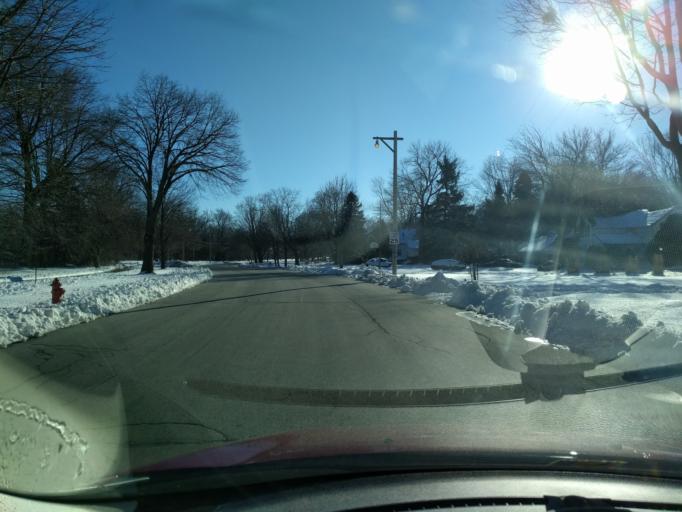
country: US
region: Wisconsin
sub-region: Milwaukee County
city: Glendale
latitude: 43.1140
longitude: -87.9257
